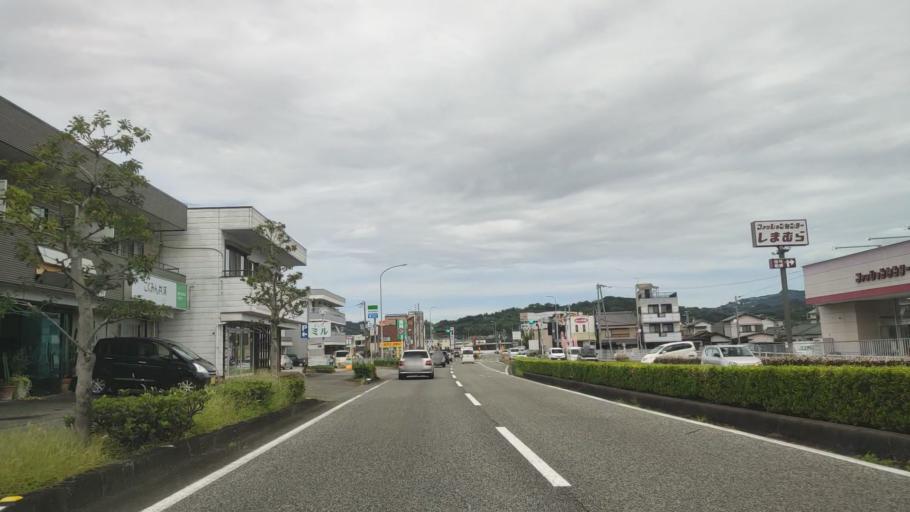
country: JP
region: Wakayama
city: Tanabe
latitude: 33.7387
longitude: 135.3947
